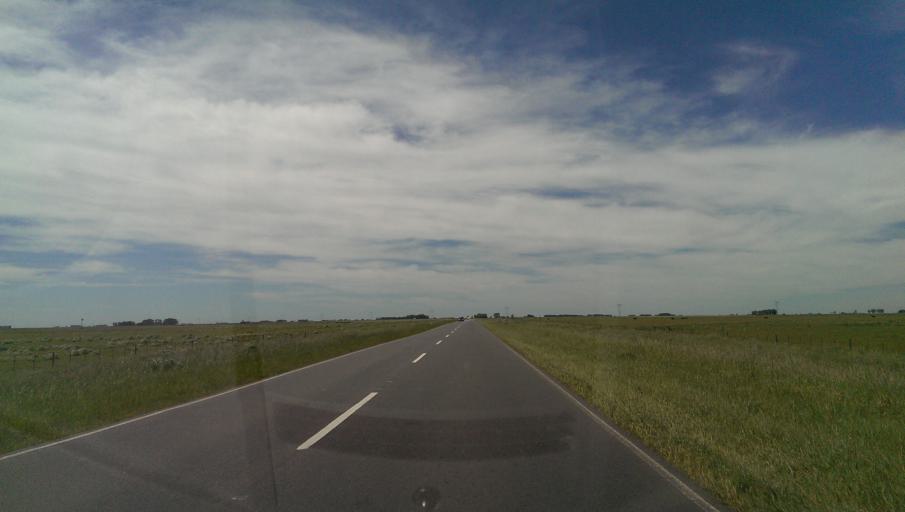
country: AR
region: Buenos Aires
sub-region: Partido de Laprida
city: Laprida
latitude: -37.2385
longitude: -60.7481
